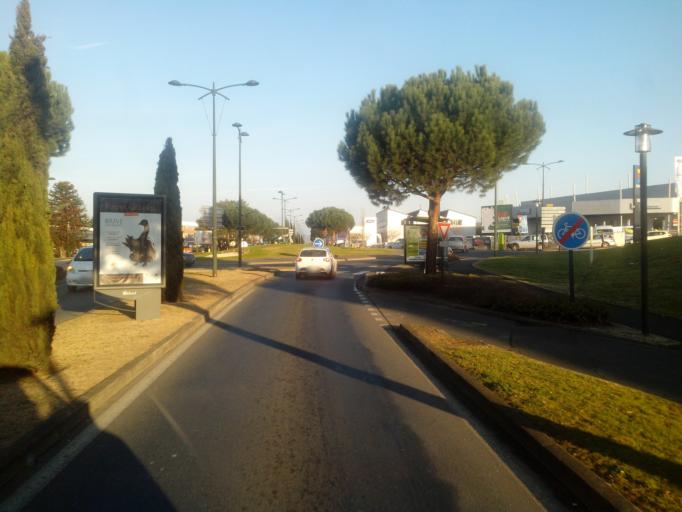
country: FR
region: Limousin
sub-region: Departement de la Correze
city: Saint-Pantaleon-de-Larche
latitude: 45.1480
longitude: 1.4889
